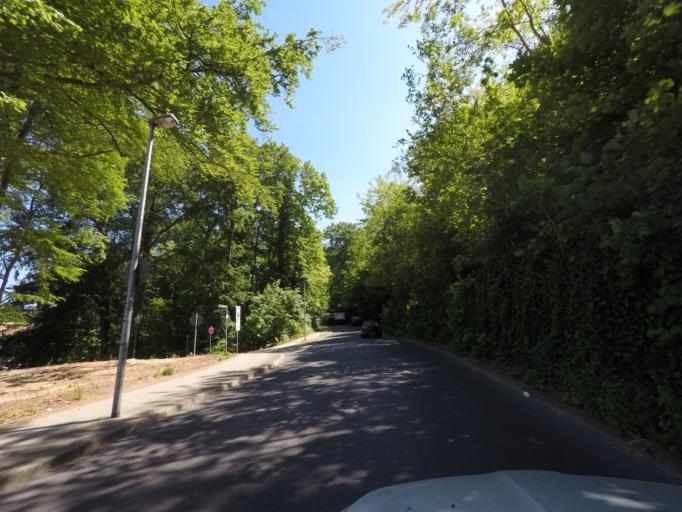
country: DE
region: Brandenburg
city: Eberswalde
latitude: 52.8289
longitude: 13.8153
